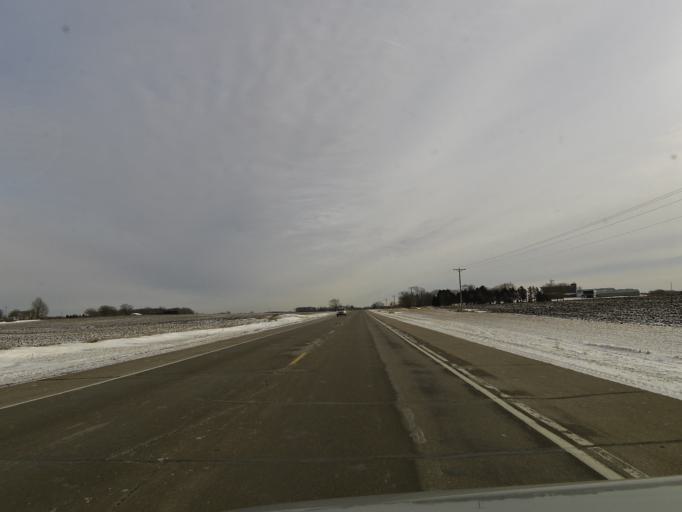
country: US
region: Minnesota
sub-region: Scott County
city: Jordan
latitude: 44.6813
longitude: -93.5384
